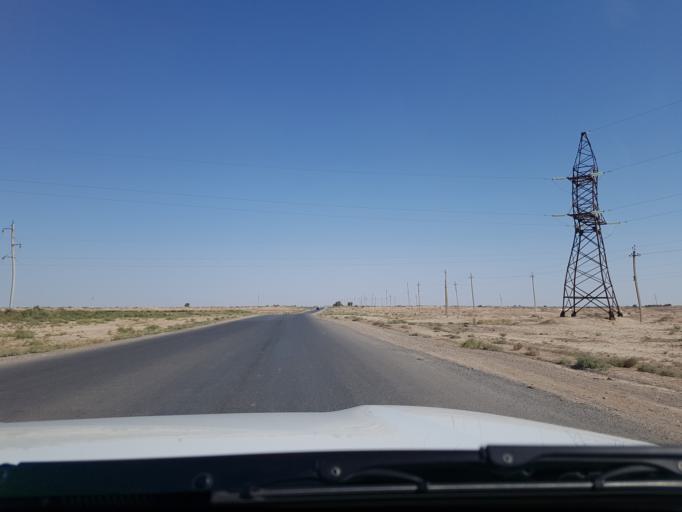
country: IR
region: Razavi Khorasan
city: Sarakhs
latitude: 36.5238
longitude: 61.2376
